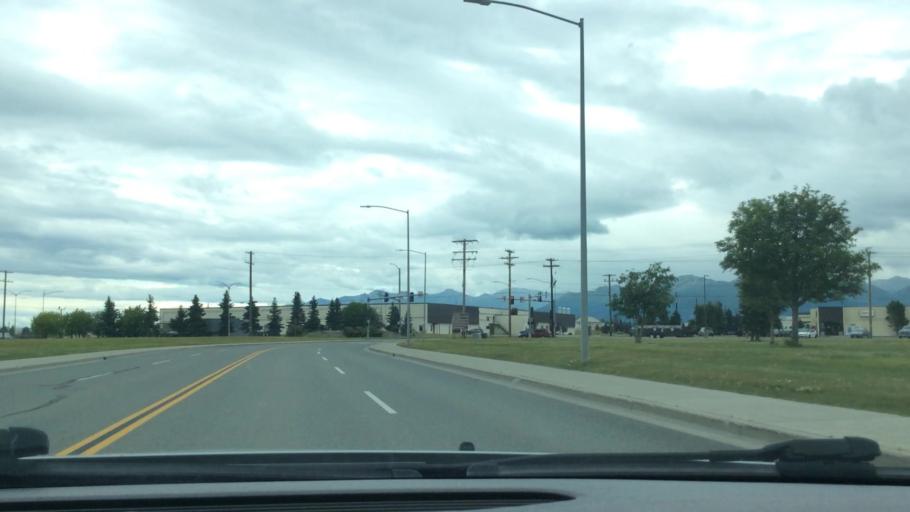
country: US
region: Alaska
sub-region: Anchorage Municipality
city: Anchorage
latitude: 61.2368
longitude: -149.8515
